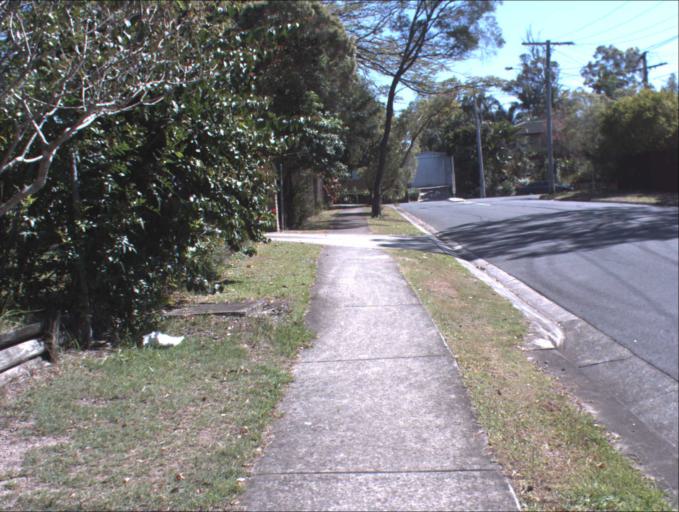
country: AU
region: Queensland
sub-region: Logan
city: Springwood
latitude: -27.6058
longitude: 153.1221
